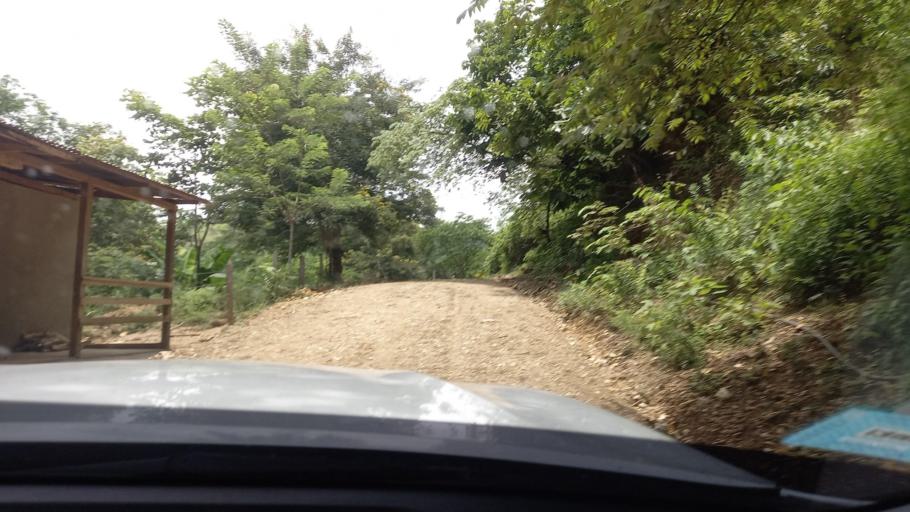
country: NI
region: Nueva Segovia
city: Wiwili
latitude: 13.7316
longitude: -85.7866
